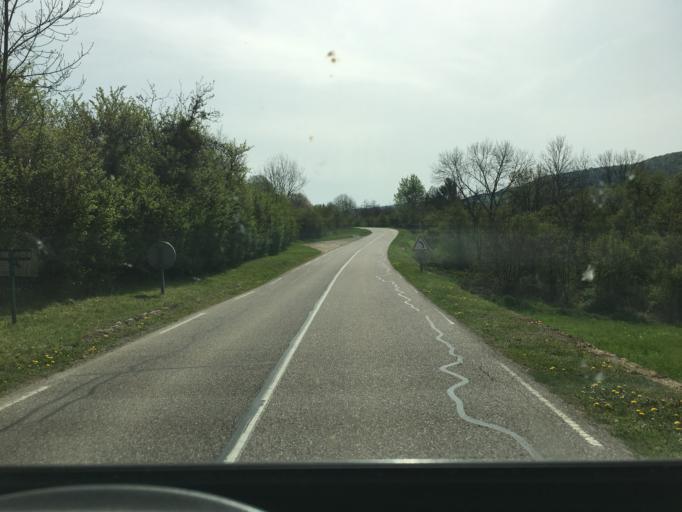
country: FR
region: Lorraine
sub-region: Departement de Meurthe-et-Moselle
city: Chaligny
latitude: 48.6282
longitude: 6.0550
